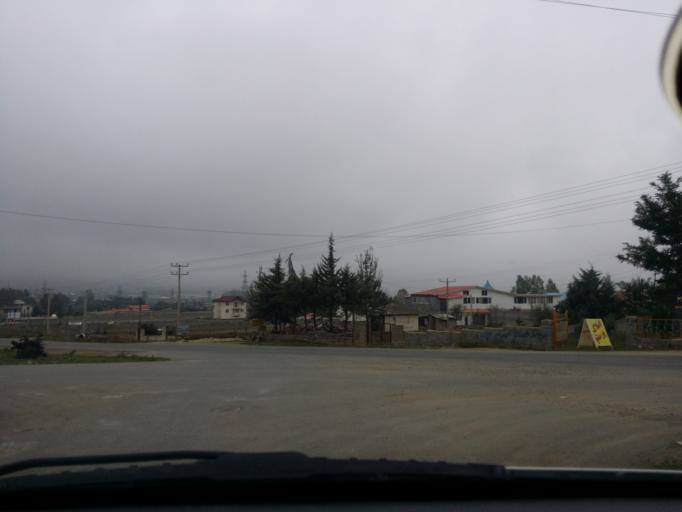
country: IR
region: Mazandaran
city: Chalus
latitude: 36.5140
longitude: 51.2262
